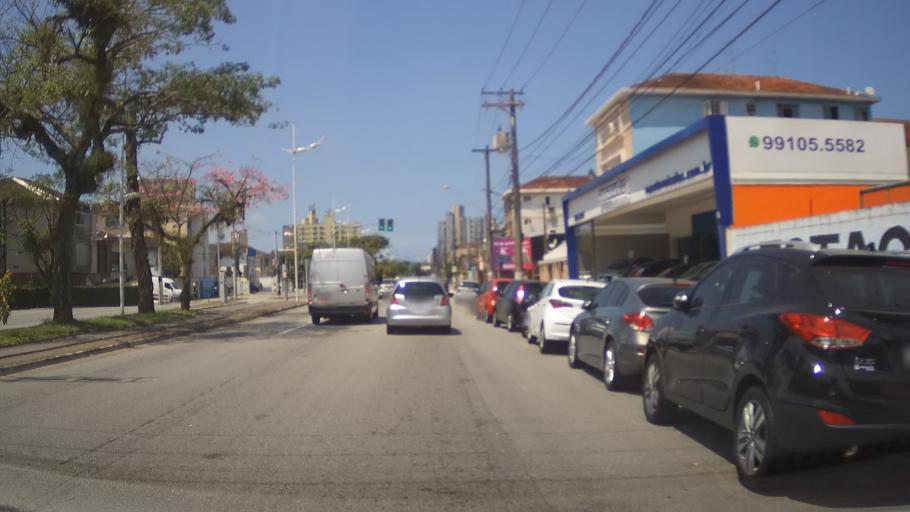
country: BR
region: Sao Paulo
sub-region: Santos
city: Santos
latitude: -23.9586
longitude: -46.3207
